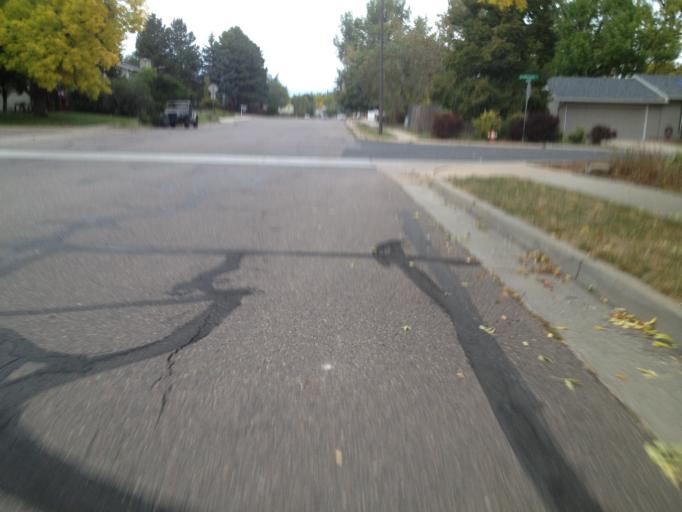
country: US
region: Colorado
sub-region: Boulder County
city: Louisville
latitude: 39.9889
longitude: -105.1384
